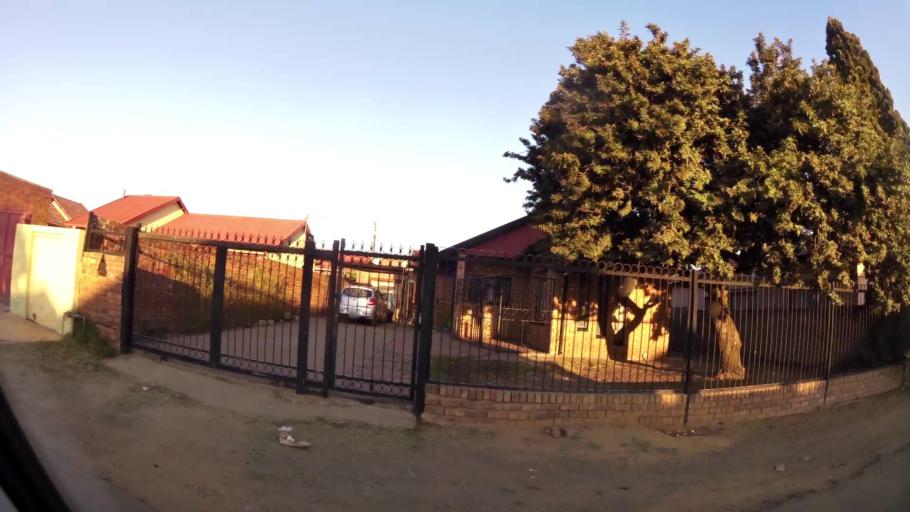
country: ZA
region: Gauteng
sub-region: City of Tshwane Metropolitan Municipality
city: Cullinan
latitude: -25.7205
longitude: 28.3911
